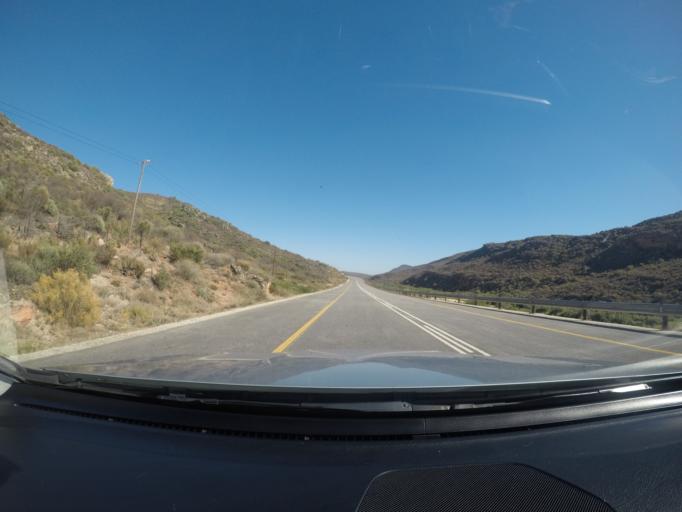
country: ZA
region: Western Cape
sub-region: West Coast District Municipality
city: Clanwilliam
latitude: -32.4116
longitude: 18.9580
